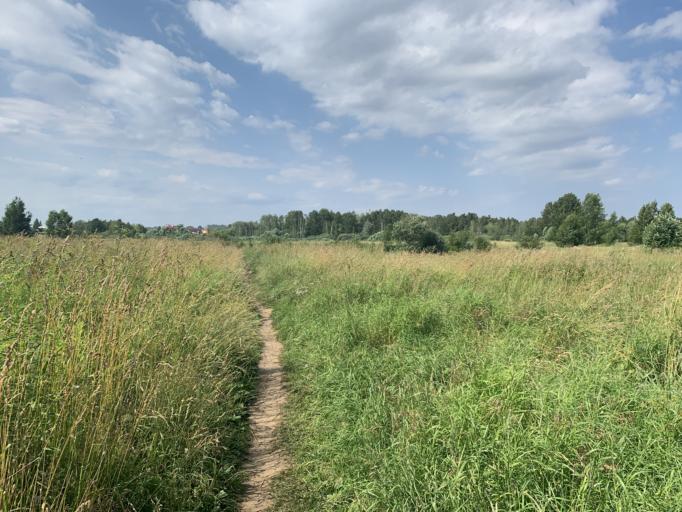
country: RU
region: Moskovskaya
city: Cherkizovo
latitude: 55.9752
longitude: 37.8002
